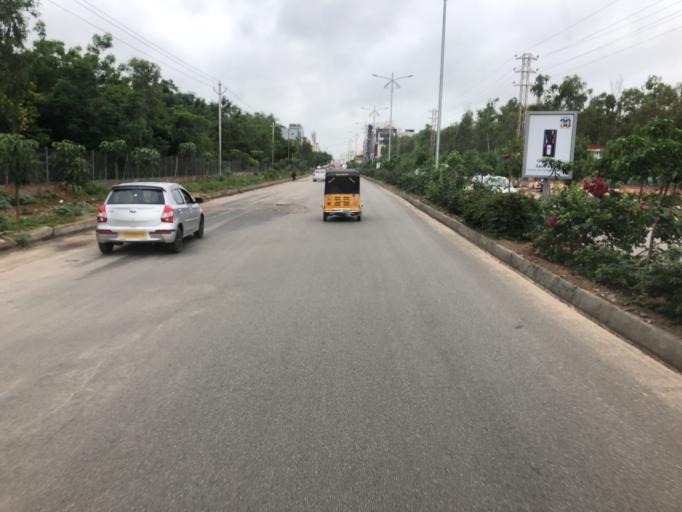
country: IN
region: Telangana
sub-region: Rangareddi
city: Kukatpalli
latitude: 17.4586
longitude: 78.3578
